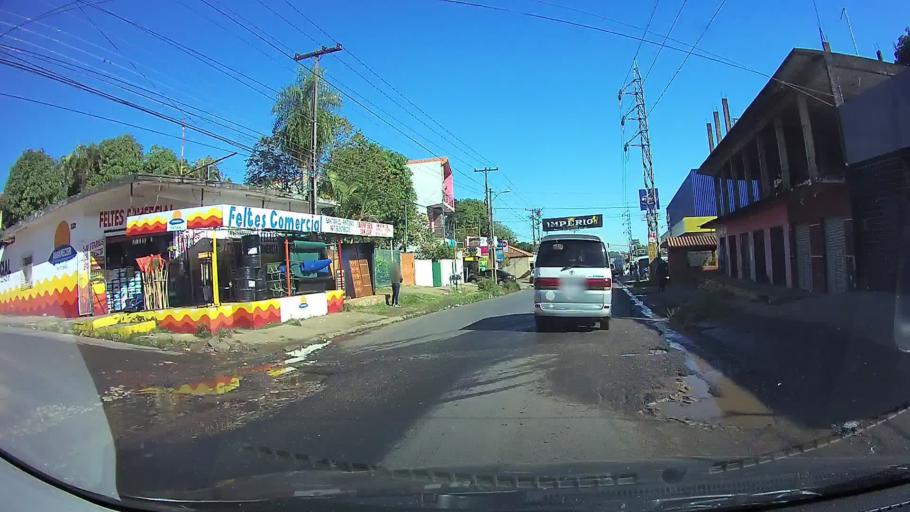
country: PY
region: Central
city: Fernando de la Mora
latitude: -25.3570
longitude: -57.5507
